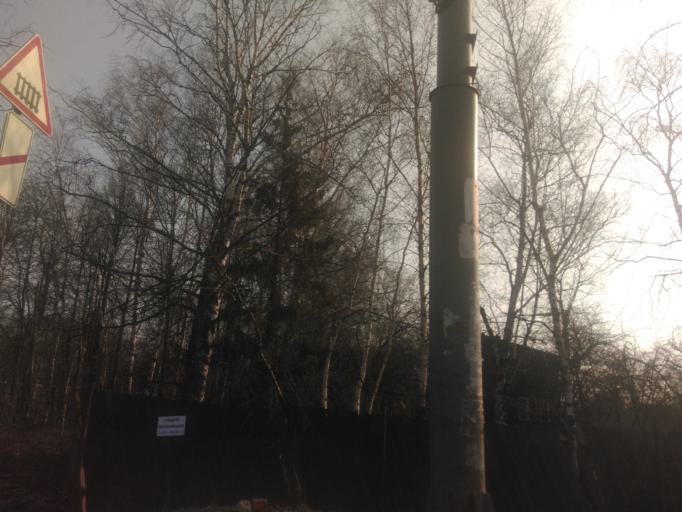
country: RU
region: Moskovskaya
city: Kokoshkino
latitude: 55.5824
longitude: 37.1240
